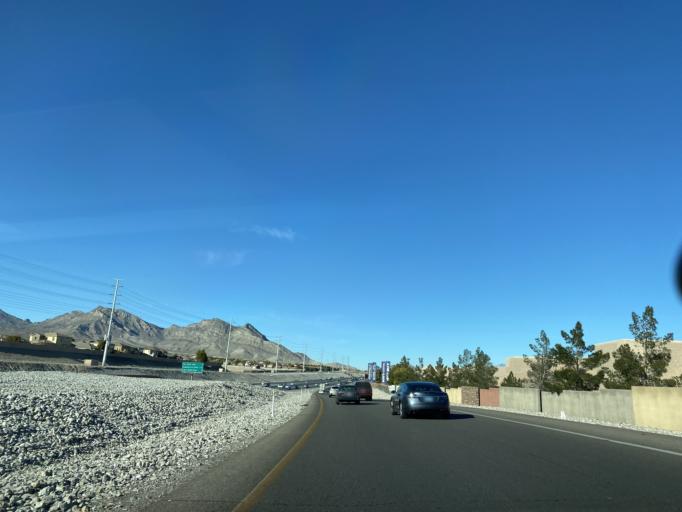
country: US
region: Nevada
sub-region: Clark County
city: Summerlin South
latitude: 36.1605
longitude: -115.3365
